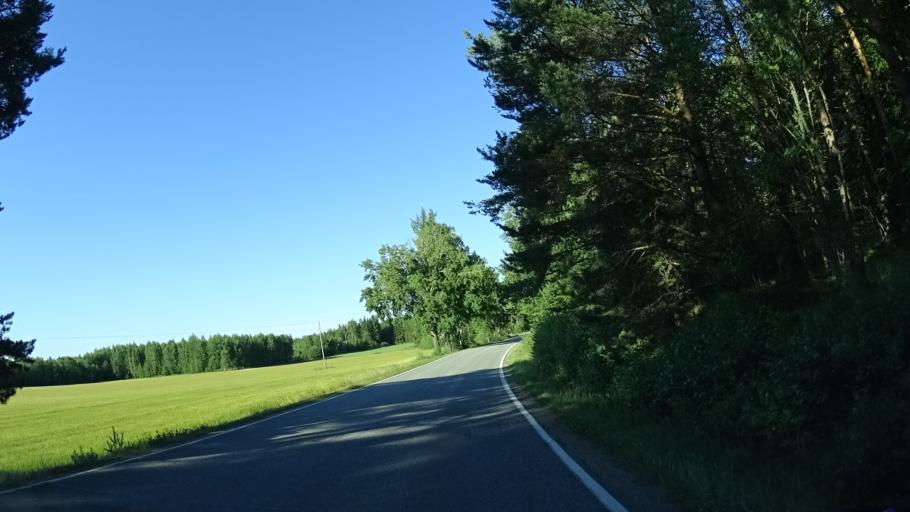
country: FI
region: Varsinais-Suomi
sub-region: Turku
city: Merimasku
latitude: 60.5014
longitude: 21.8087
